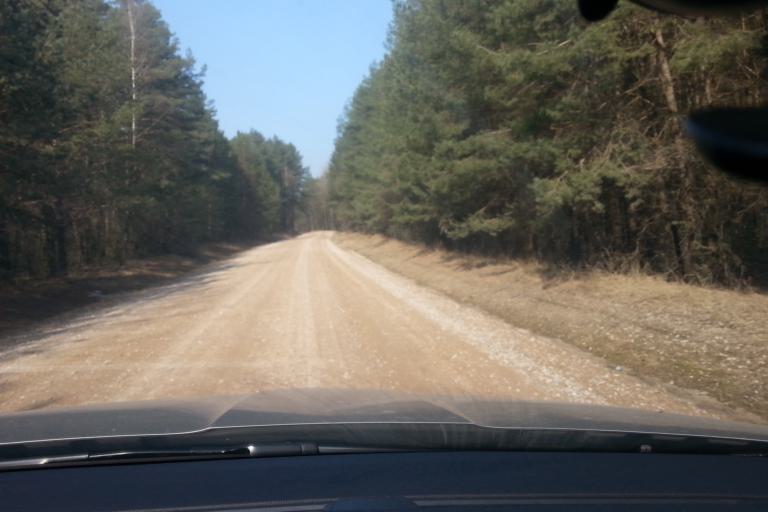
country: LT
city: Trakai
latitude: 54.5618
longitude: 24.9782
